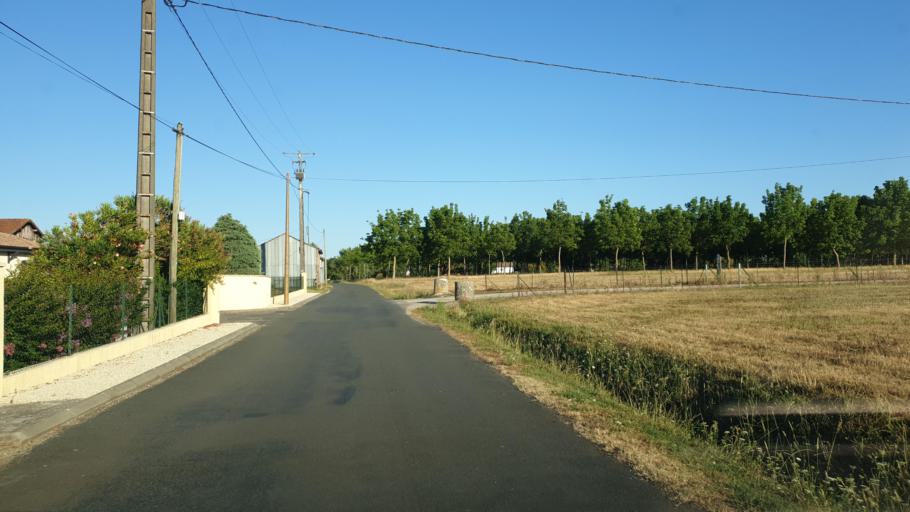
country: FR
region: Aquitaine
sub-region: Departement du Lot-et-Garonne
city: Castelmoron-sur-Lot
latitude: 44.3872
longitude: 0.5089
